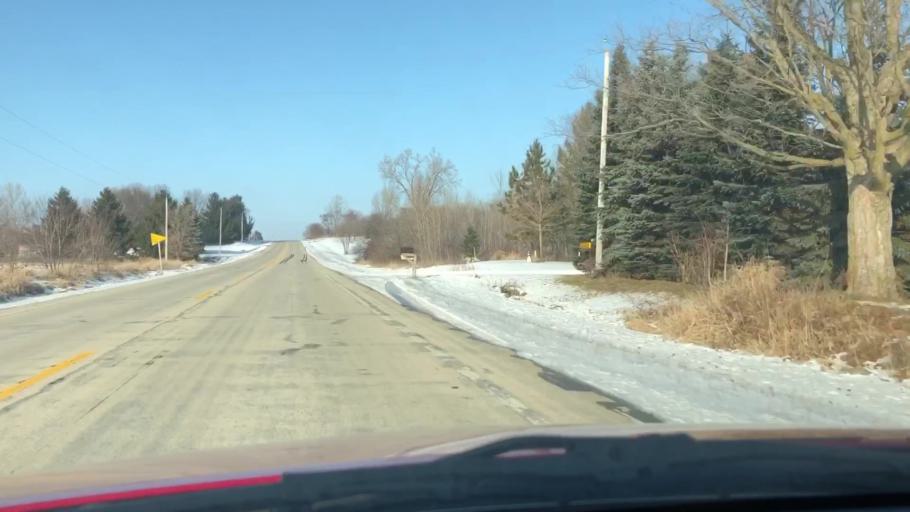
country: US
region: Wisconsin
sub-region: Outagamie County
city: Kimberly
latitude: 44.3730
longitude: -88.3748
